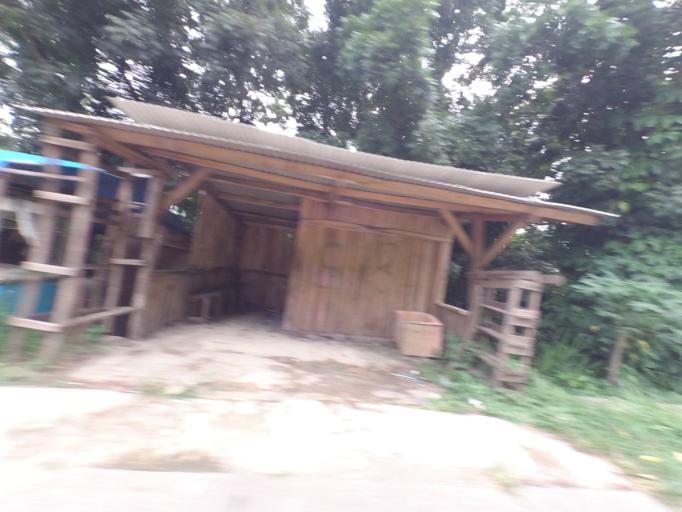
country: ID
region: West Java
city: Sidoger Lebak
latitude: -6.5609
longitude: 106.5768
